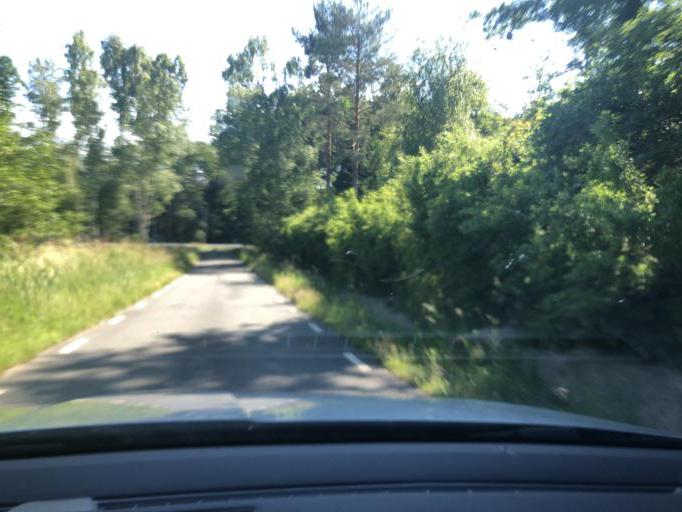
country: SE
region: Blekinge
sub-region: Karlshamns Kommun
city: Morrum
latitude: 56.1724
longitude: 14.7035
